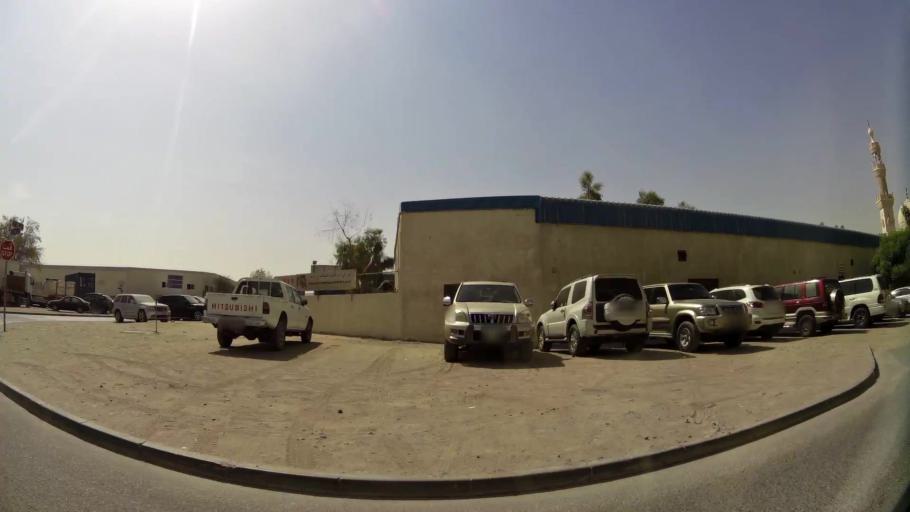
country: AE
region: Ash Shariqah
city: Sharjah
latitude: 25.2826
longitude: 55.3902
